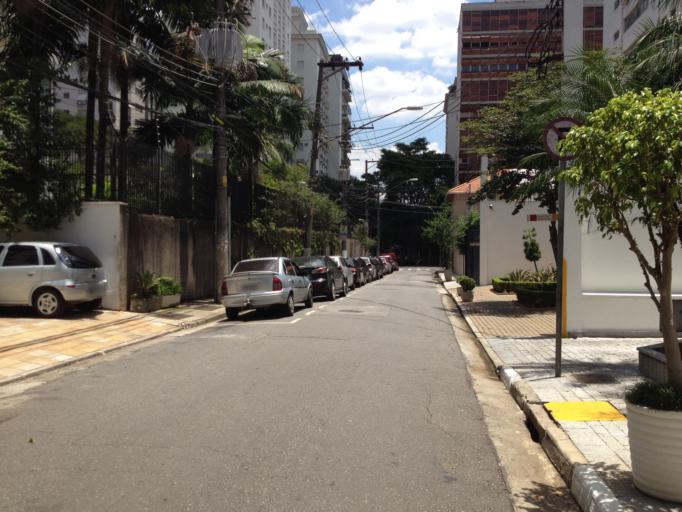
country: BR
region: Sao Paulo
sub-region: Sao Paulo
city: Sao Paulo
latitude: -23.5664
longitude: -46.6659
